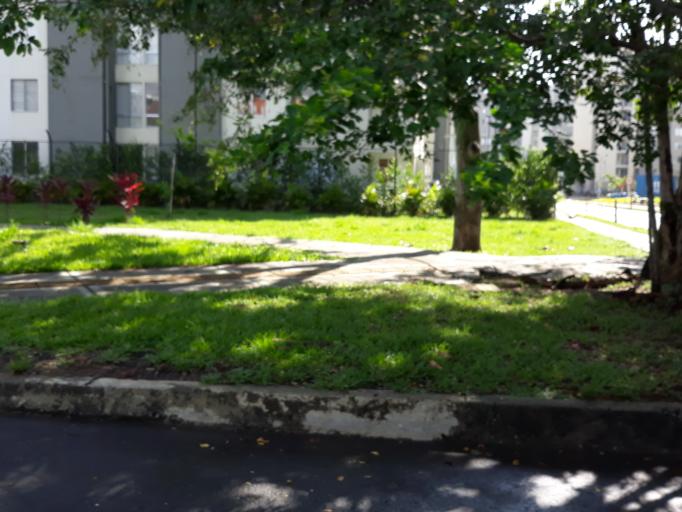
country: CO
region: Valle del Cauca
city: Cali
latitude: 3.3559
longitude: -76.5158
